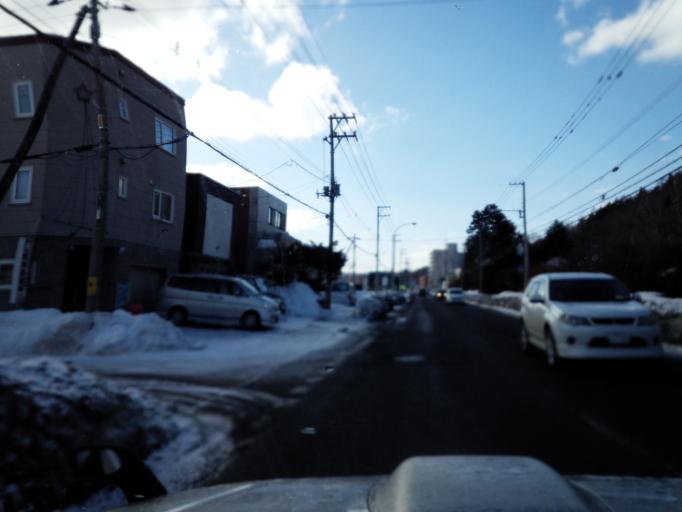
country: JP
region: Hokkaido
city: Sapporo
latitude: 42.9590
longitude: 141.3435
